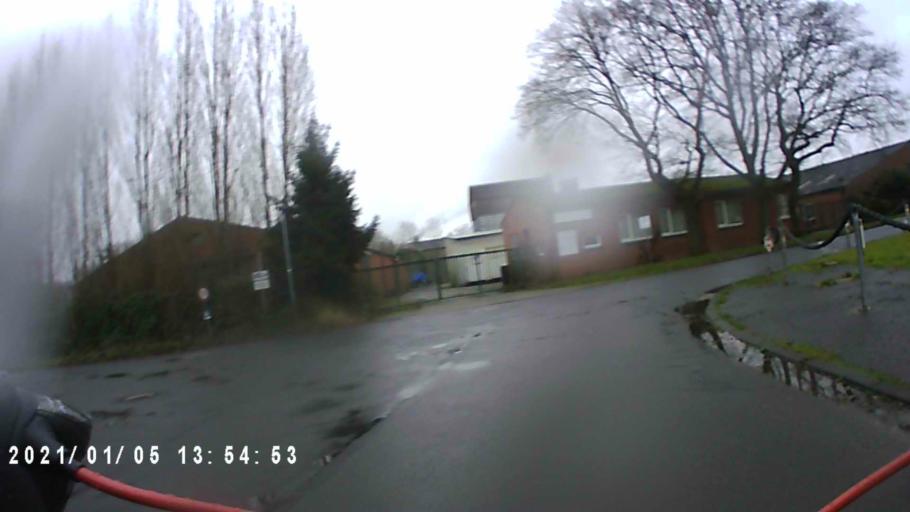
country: DE
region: Lower Saxony
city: Weener
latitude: 53.1695
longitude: 7.3617
